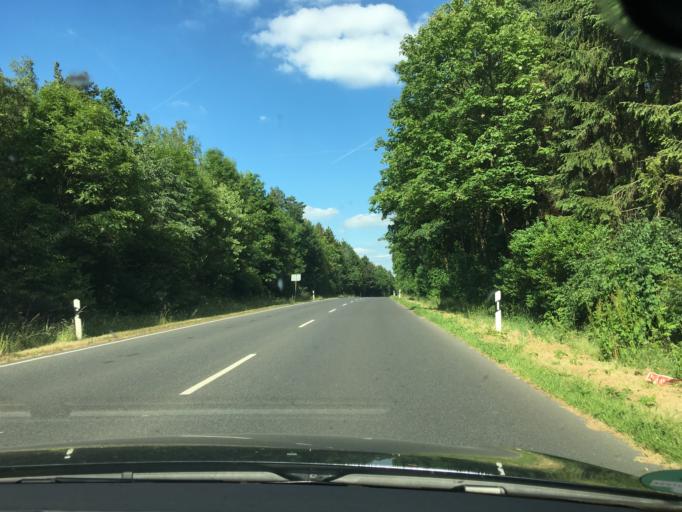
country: DE
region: North Rhine-Westphalia
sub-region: Regierungsbezirk Koln
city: Kreuzau
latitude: 50.7353
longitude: 6.4477
